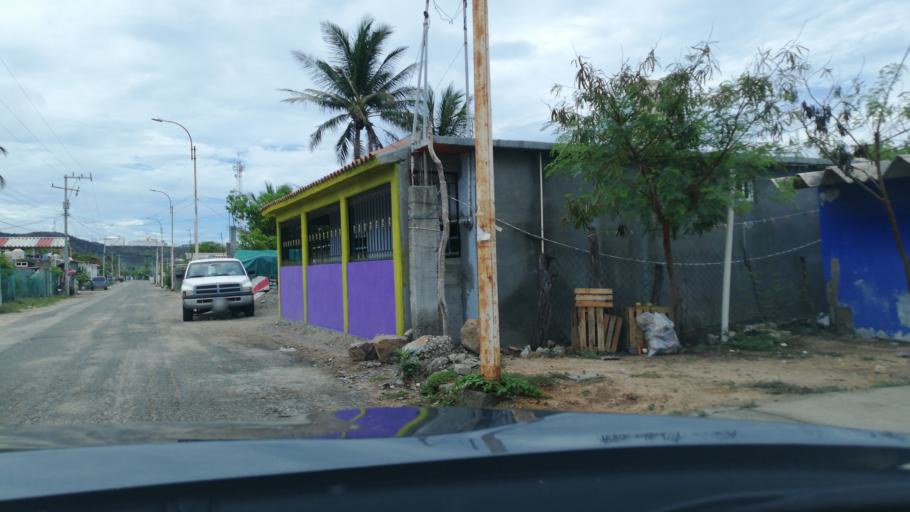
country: MX
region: Oaxaca
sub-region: Salina Cruz
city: Salina Cruz
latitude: 16.1625
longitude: -95.2252
